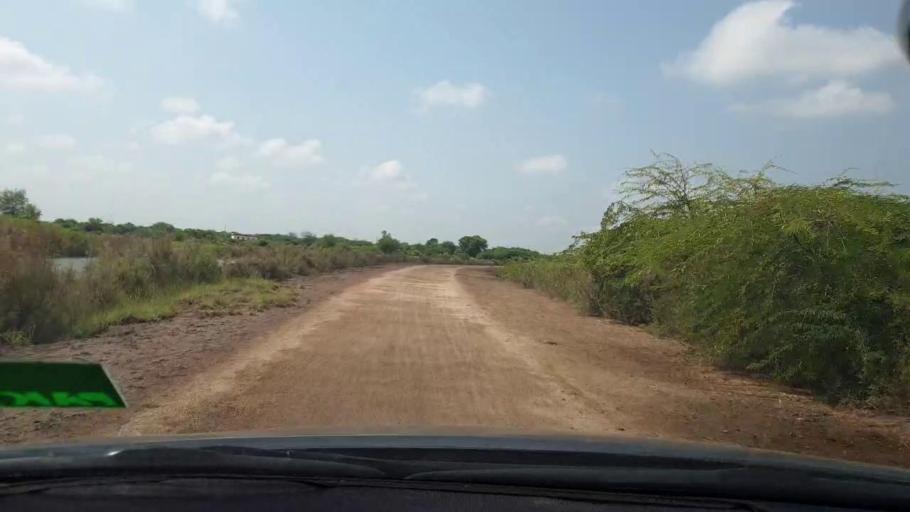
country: PK
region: Sindh
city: Tando Bago
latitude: 24.9318
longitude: 69.0447
